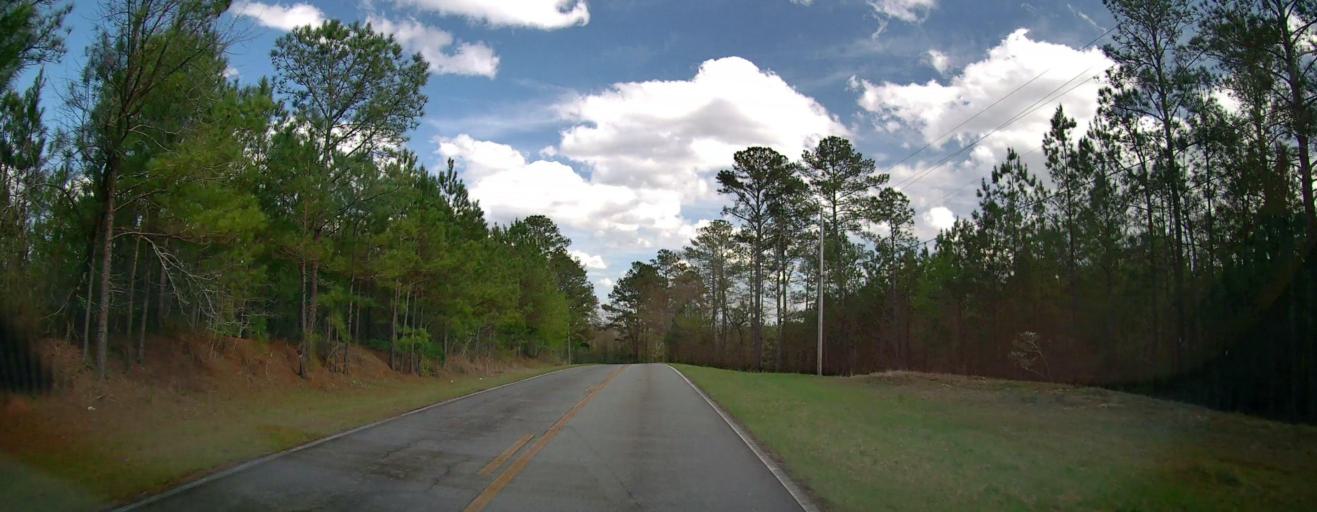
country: US
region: Georgia
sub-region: Wilkinson County
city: Gordon
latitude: 32.8016
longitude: -83.4248
